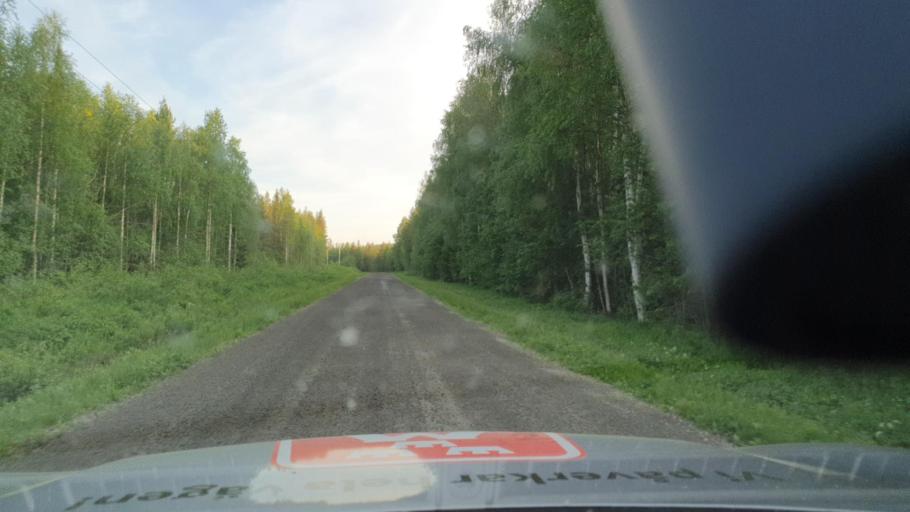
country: SE
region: Norrbotten
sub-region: Bodens Kommun
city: Boden
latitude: 66.1444
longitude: 21.5648
